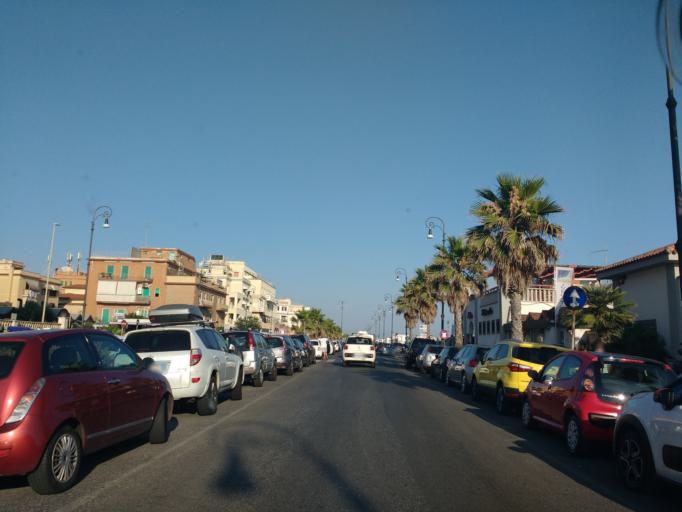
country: IT
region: Latium
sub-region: Citta metropolitana di Roma Capitale
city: Lido di Ostia
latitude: 41.7304
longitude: 12.2742
